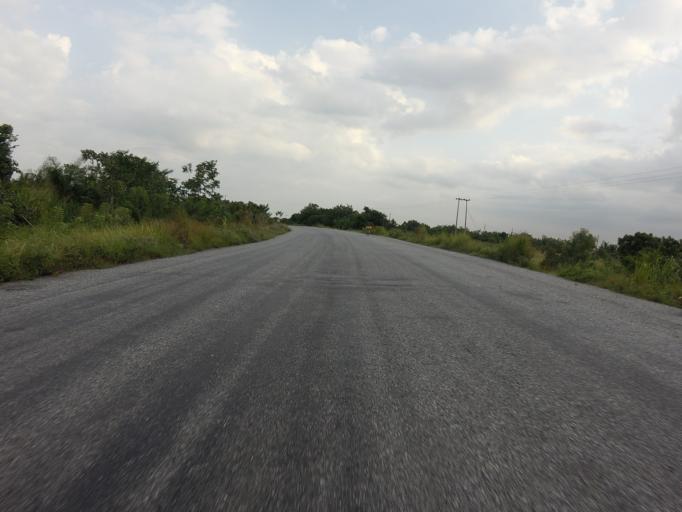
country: GH
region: Volta
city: Ho
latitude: 6.3707
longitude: 0.5334
